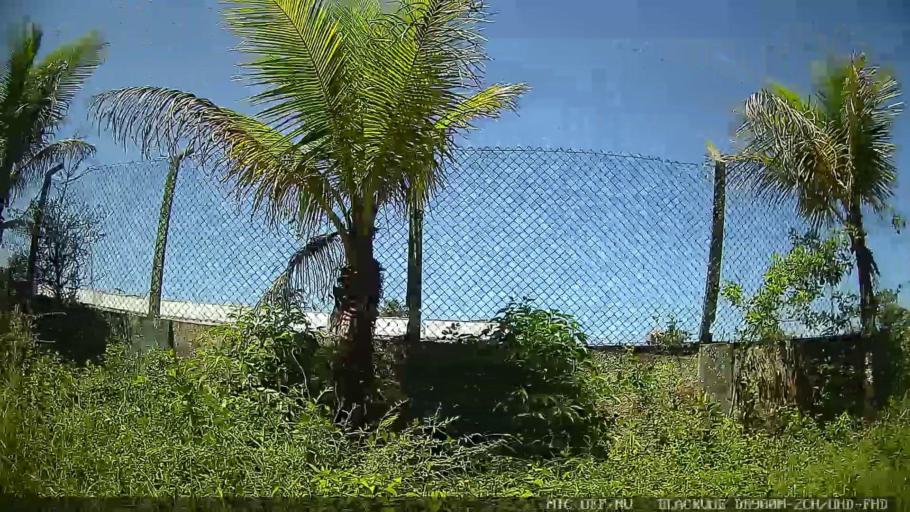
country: BR
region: Sao Paulo
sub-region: Peruibe
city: Peruibe
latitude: -24.2980
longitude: -46.9975
